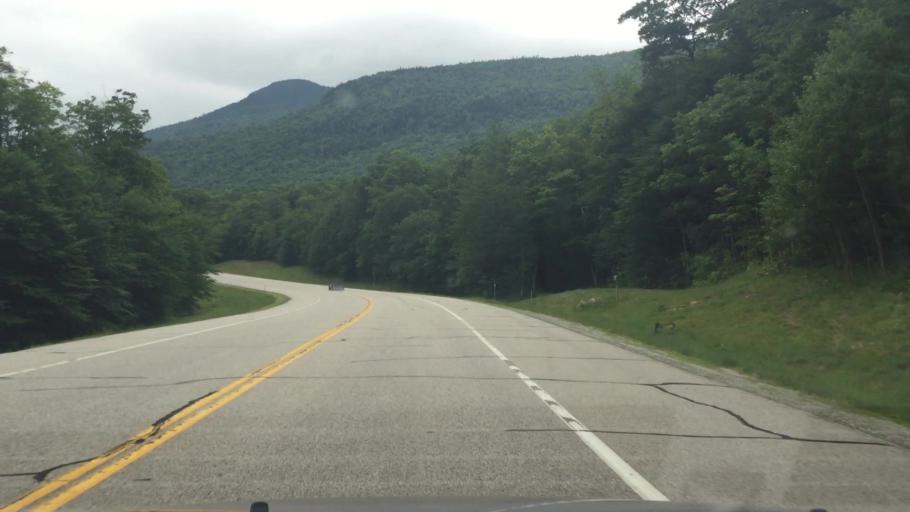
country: US
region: New Hampshire
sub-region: Carroll County
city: North Conway
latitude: 44.1521
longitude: -71.3655
